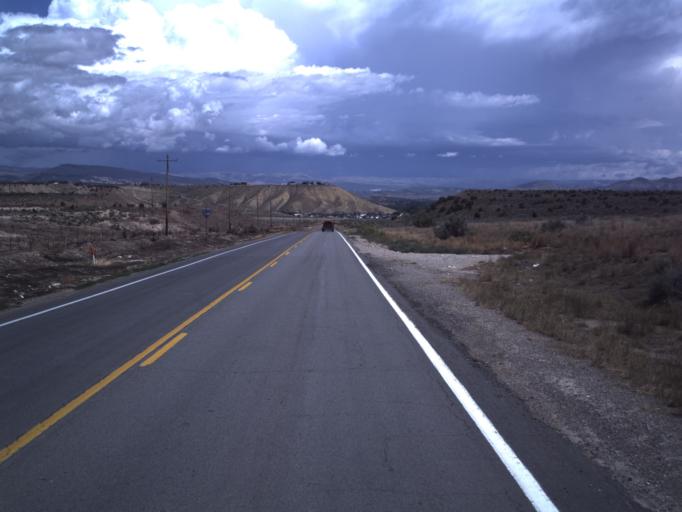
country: US
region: Utah
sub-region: Uintah County
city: Maeser
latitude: 40.4518
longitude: -109.6223
